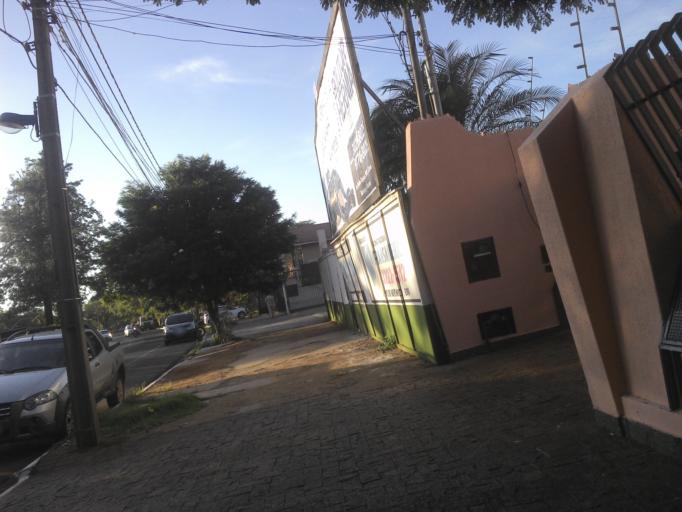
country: BR
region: Parana
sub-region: Maringa
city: Maringa
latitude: -23.4262
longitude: -51.9401
